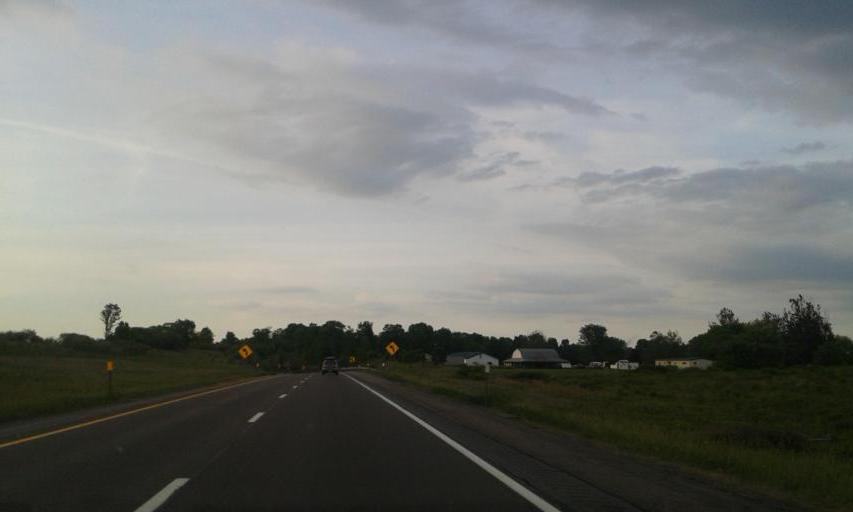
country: US
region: New York
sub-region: Broome County
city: Chenango Bridge
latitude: 42.2882
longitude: -75.9243
